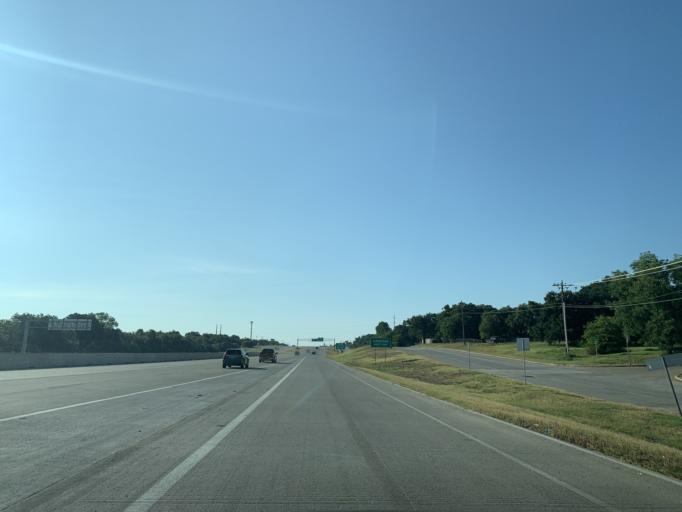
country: US
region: Texas
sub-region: Tarrant County
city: Lakeside
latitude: 32.8344
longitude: -97.4884
